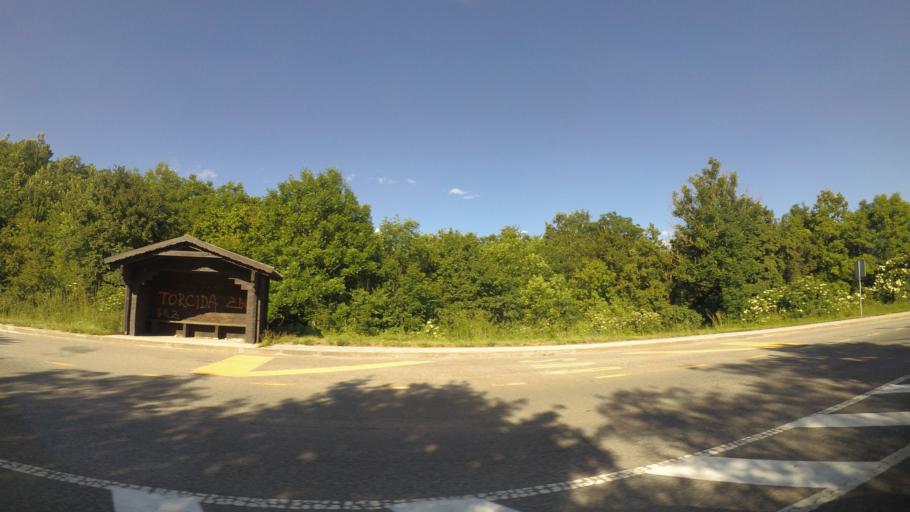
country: BA
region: Federation of Bosnia and Herzegovina
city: Bihac
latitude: 44.7058
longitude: 15.7483
